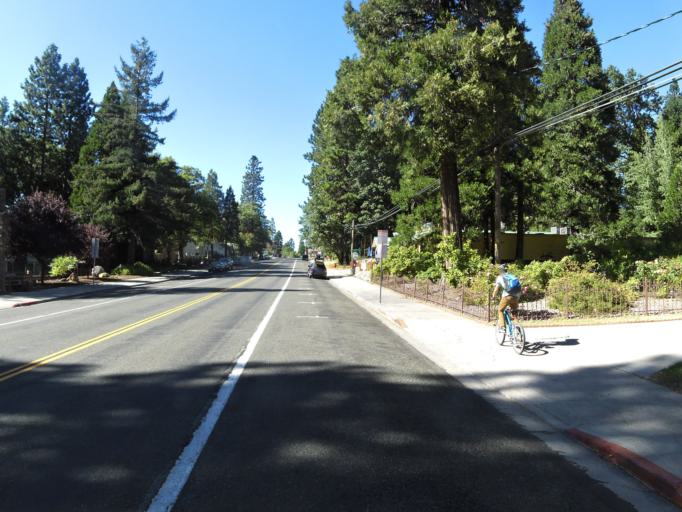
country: US
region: California
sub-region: Siskiyou County
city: Mount Shasta
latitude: 41.3036
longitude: -122.3081
